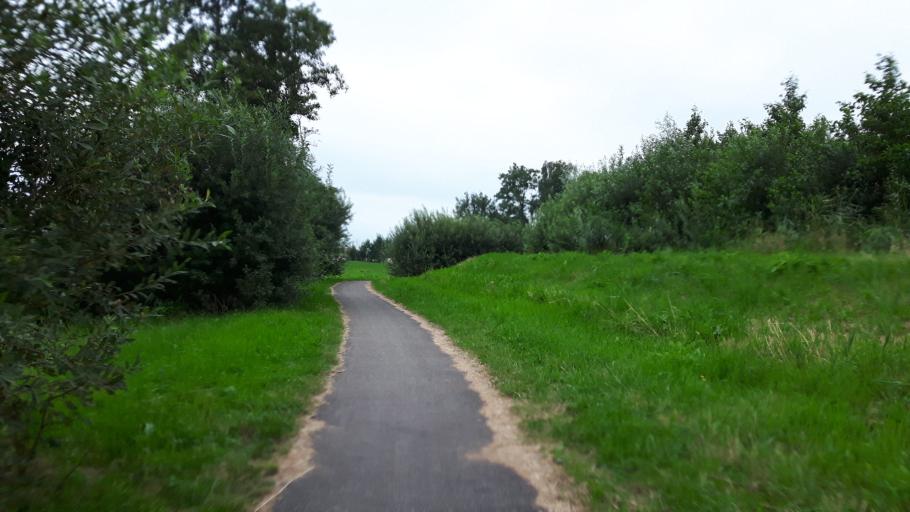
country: NL
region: South Holland
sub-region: Gemeente Kaag en Braassem
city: Oude Wetering
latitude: 52.1693
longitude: 4.6061
